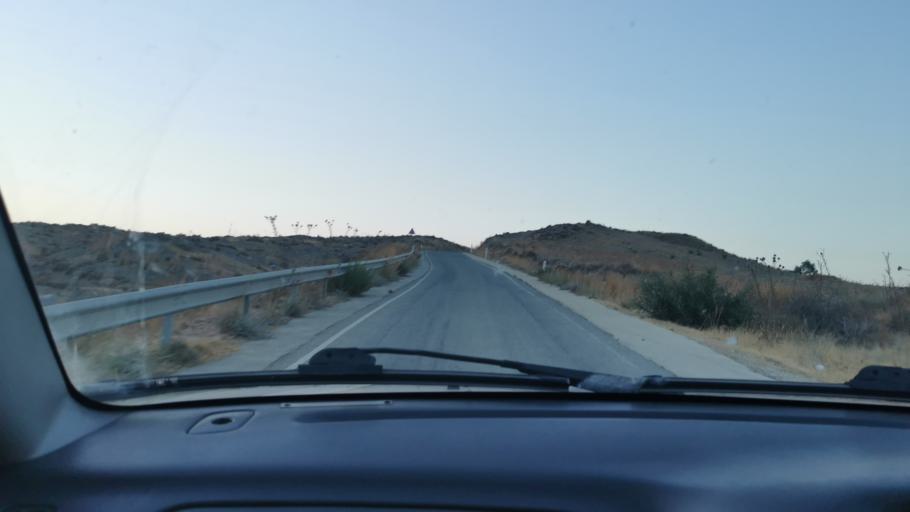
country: CY
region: Lefkosia
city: Peristerona
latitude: 35.0715
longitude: 33.0808
